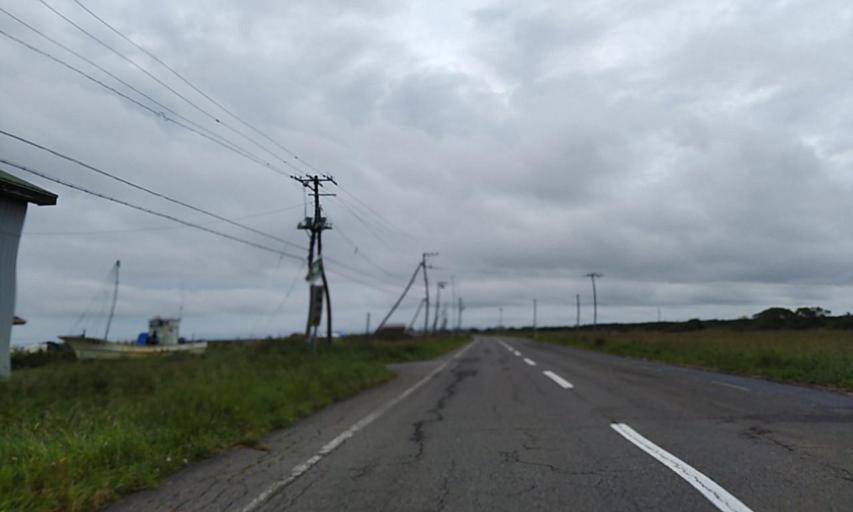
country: JP
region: Hokkaido
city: Shibetsu
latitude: 43.3961
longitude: 145.2801
